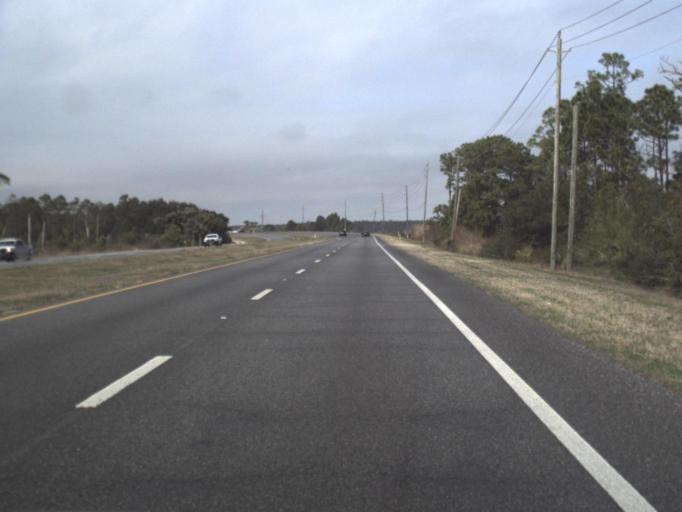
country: US
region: Florida
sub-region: Bay County
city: Laguna Beach
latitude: 30.2681
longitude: -85.9793
